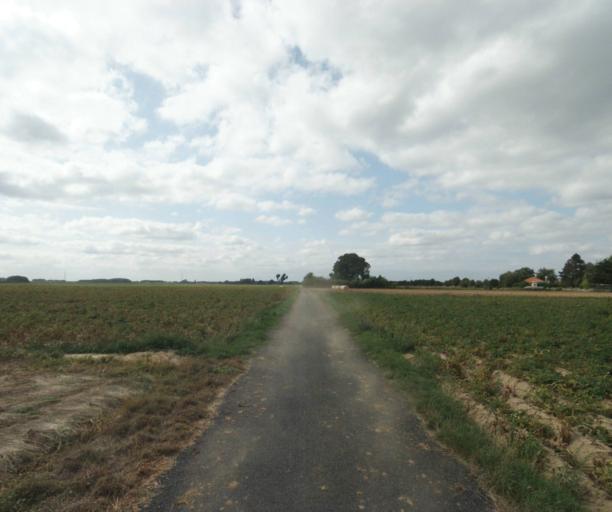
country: FR
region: Nord-Pas-de-Calais
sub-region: Departement du Nord
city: Baisieux
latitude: 50.6046
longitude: 3.2453
